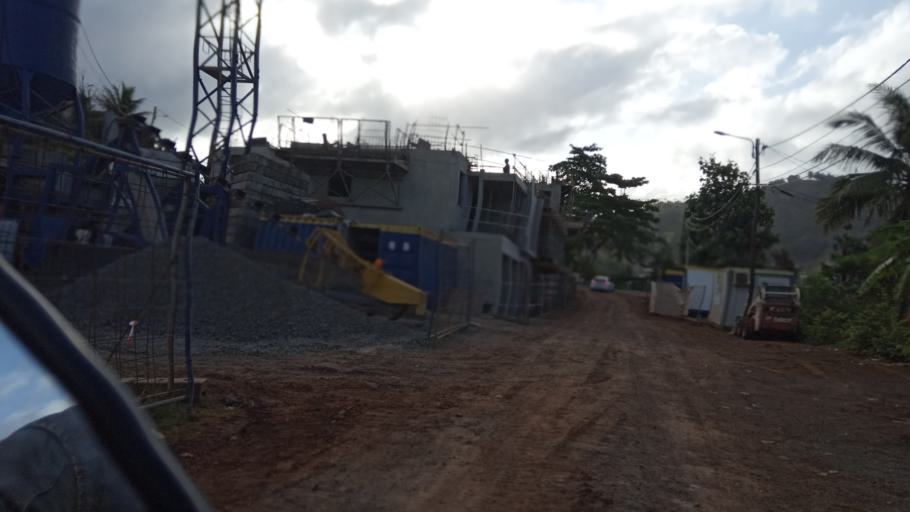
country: YT
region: Mamoudzou
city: Mamoudzou
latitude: -12.7847
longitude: 45.2237
